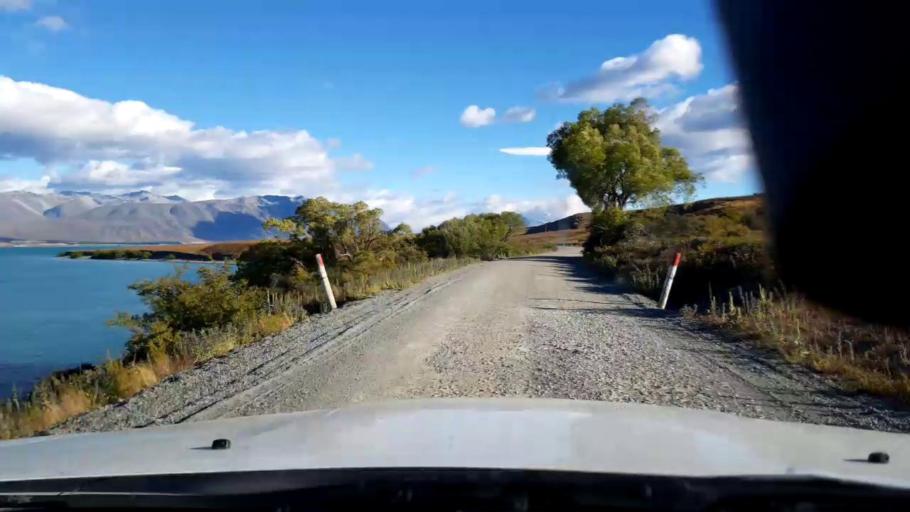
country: NZ
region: Canterbury
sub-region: Timaru District
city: Pleasant Point
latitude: -43.9277
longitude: 170.5604
